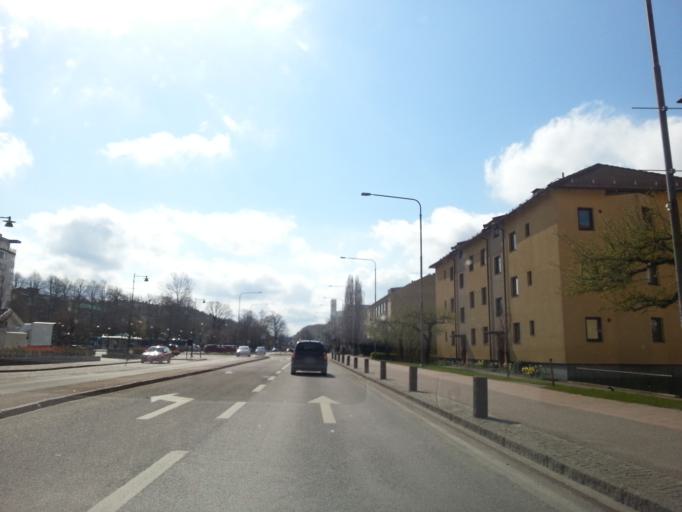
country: SE
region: Vaestra Goetaland
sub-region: Kungalvs Kommun
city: Kungalv
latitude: 57.8733
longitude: 11.9776
